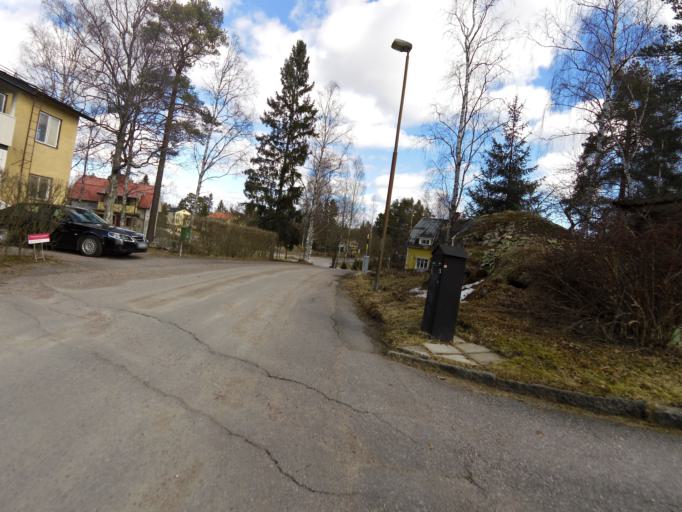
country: SE
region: Gaevleborg
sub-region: Hofors Kommun
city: Hofors
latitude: 60.5364
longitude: 16.2991
